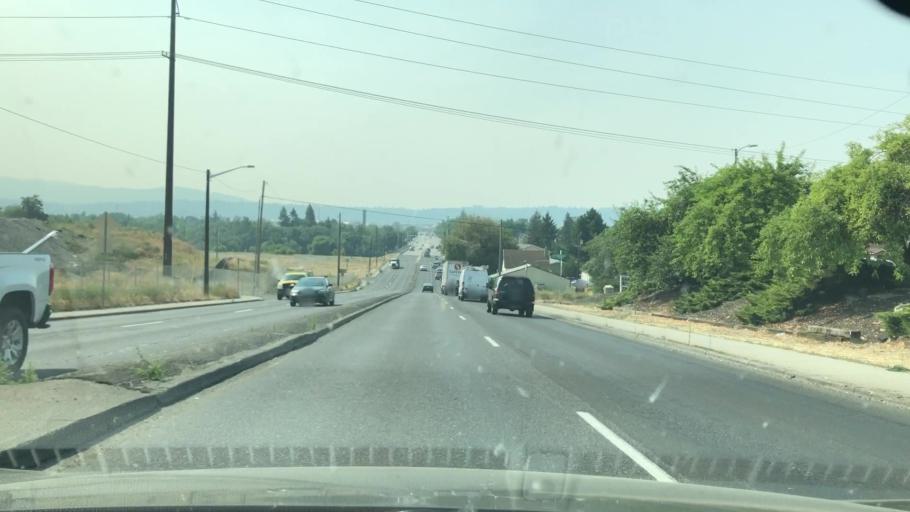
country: US
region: Washington
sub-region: Spokane County
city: Spokane
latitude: 47.6822
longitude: -117.3636
